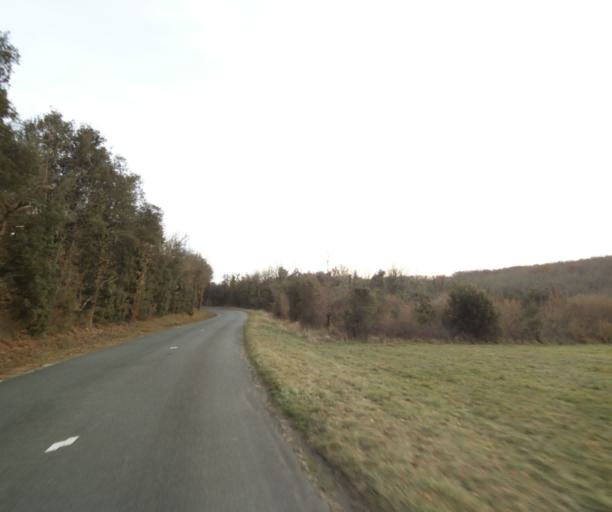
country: FR
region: Poitou-Charentes
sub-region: Departement de la Charente-Maritime
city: Fontcouverte
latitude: 45.8117
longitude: -0.5936
